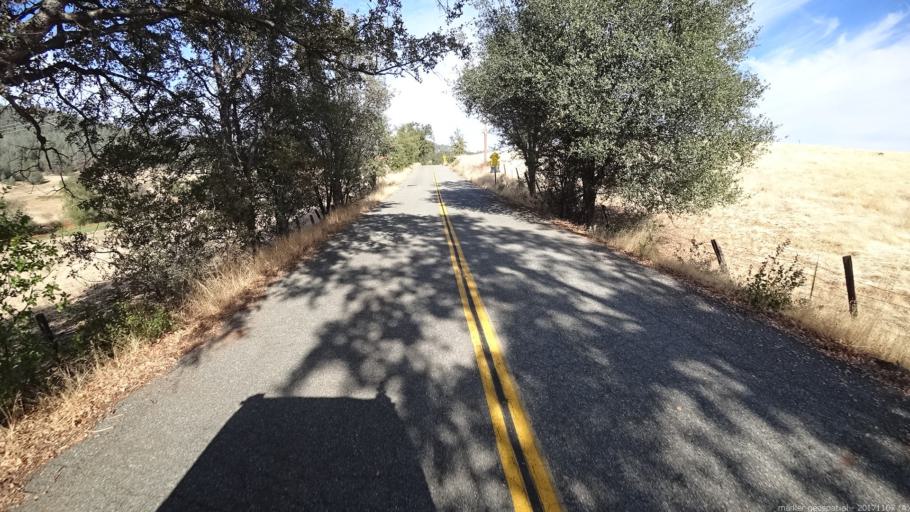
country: US
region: California
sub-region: Shasta County
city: Shasta
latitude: 40.5051
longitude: -122.5471
